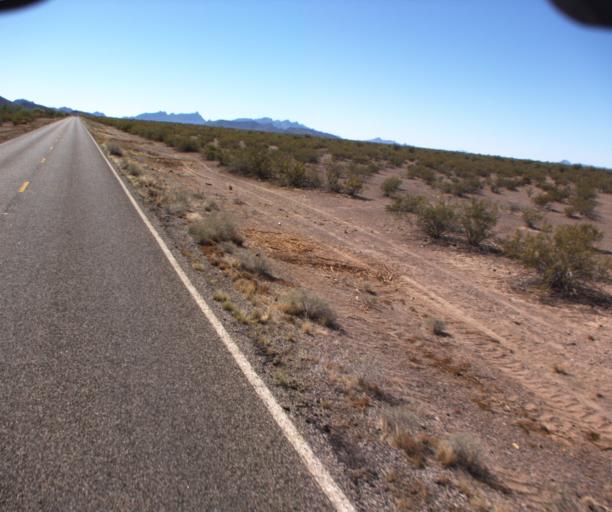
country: US
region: Arizona
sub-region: Pima County
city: Ajo
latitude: 32.3165
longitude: -112.7674
